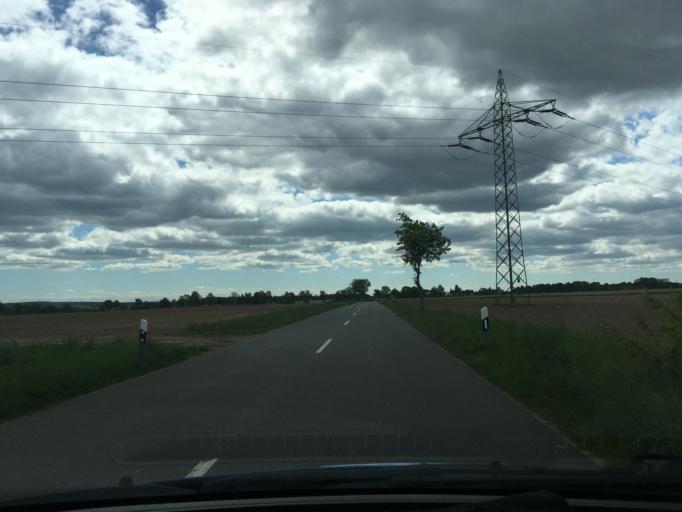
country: DE
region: Lower Saxony
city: Suderburg
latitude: 52.9170
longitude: 10.4393
